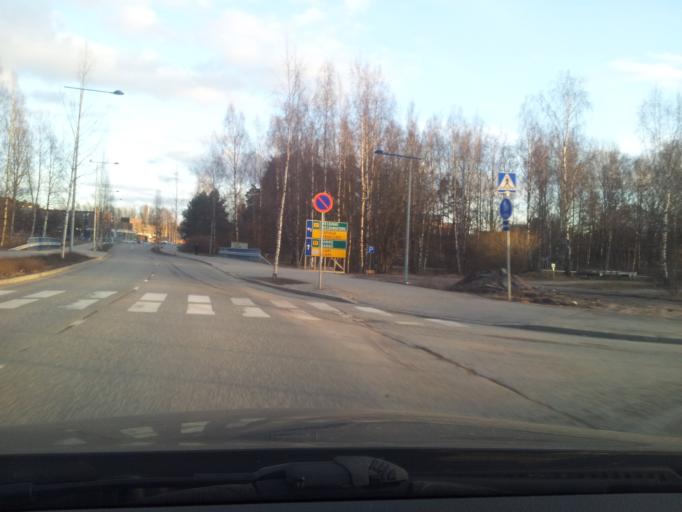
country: FI
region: Uusimaa
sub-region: Helsinki
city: Koukkuniemi
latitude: 60.1743
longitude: 24.7591
